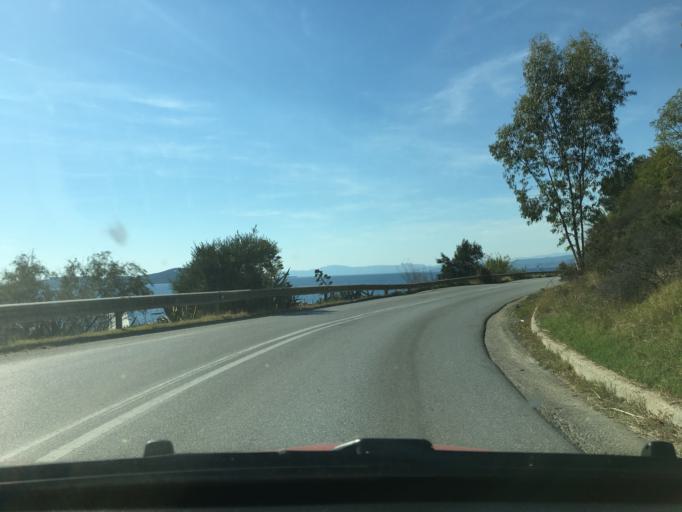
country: GR
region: Central Macedonia
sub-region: Nomos Chalkidikis
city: Nea Roda
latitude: 40.3542
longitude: 23.9497
